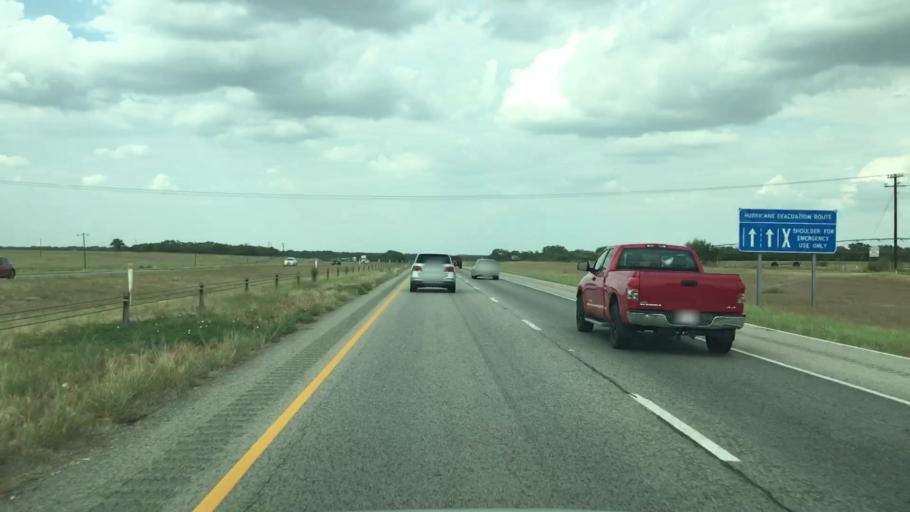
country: US
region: Texas
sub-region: Atascosa County
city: Pleasanton
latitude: 29.0163
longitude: -98.4310
